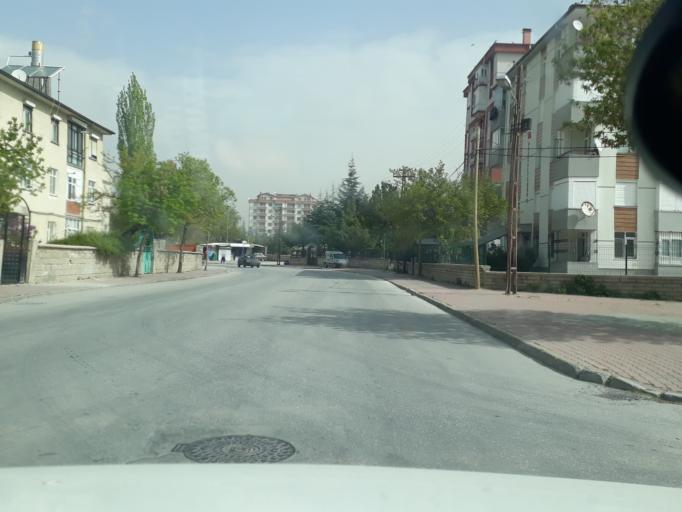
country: TR
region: Konya
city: Selcuklu
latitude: 37.9346
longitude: 32.4998
